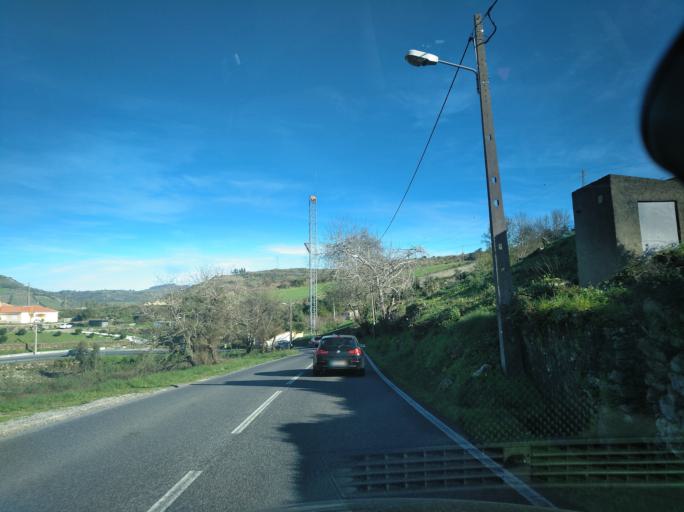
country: PT
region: Lisbon
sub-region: Sintra
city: Pero Pinheiro
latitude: 38.8839
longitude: -9.3324
